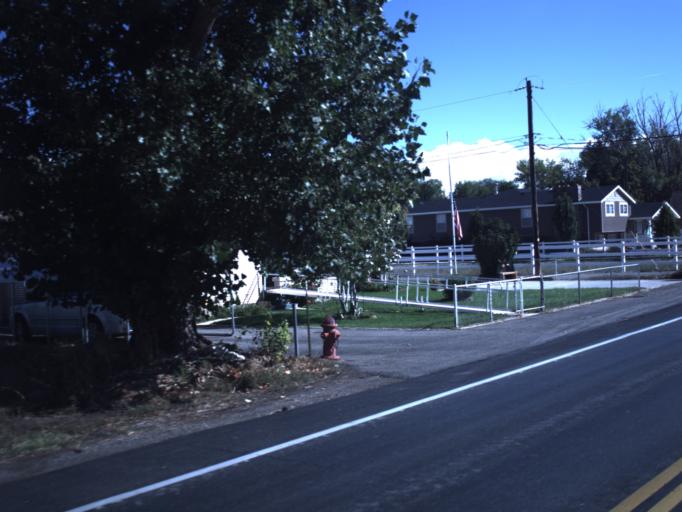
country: US
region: Utah
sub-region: Utah County
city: Spanish Fork
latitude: 40.0984
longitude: -111.6855
